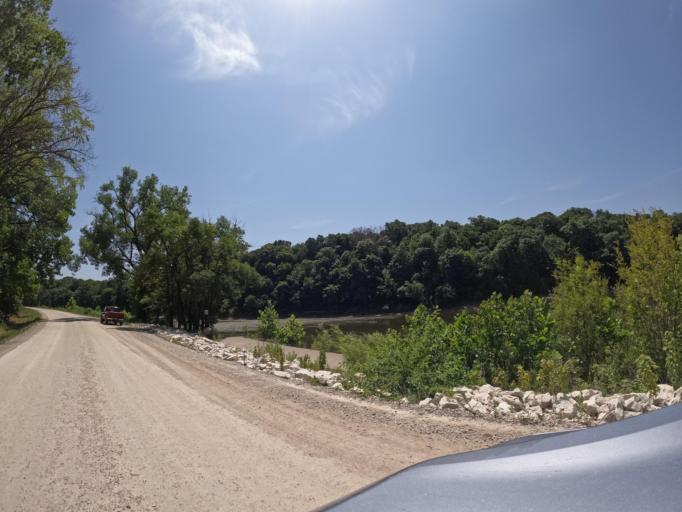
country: US
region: Iowa
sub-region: Henry County
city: Mount Pleasant
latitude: 40.9347
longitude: -91.6140
